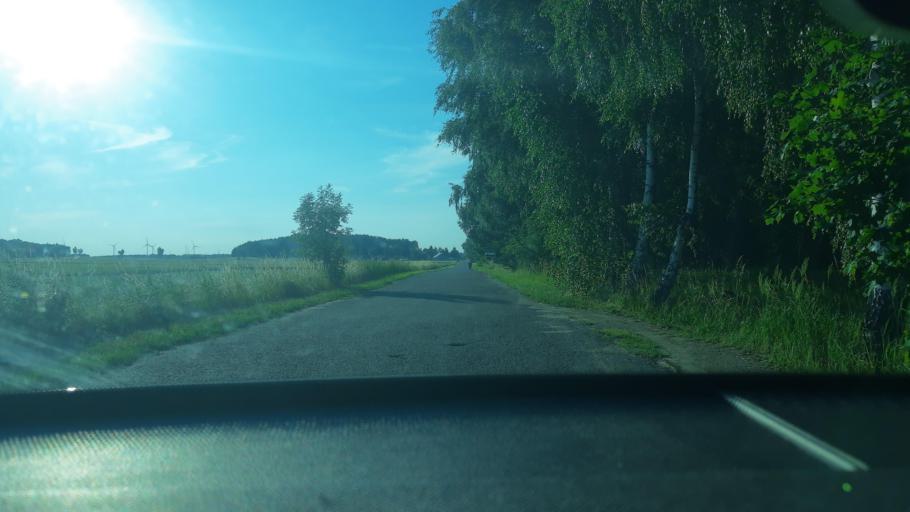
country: PL
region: Lodz Voivodeship
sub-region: Powiat sieradzki
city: Sieradz
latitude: 51.5366
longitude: 18.7660
